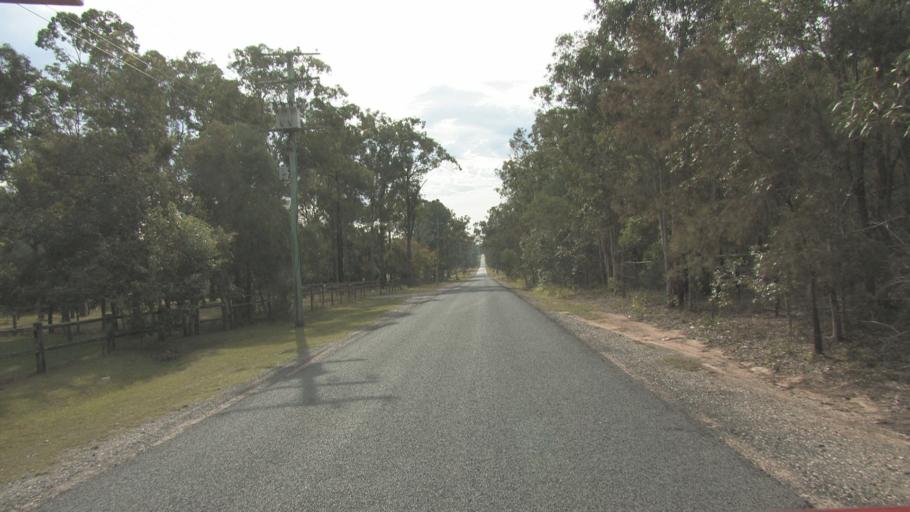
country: AU
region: Queensland
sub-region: Logan
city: Chambers Flat
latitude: -27.7931
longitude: 153.1214
